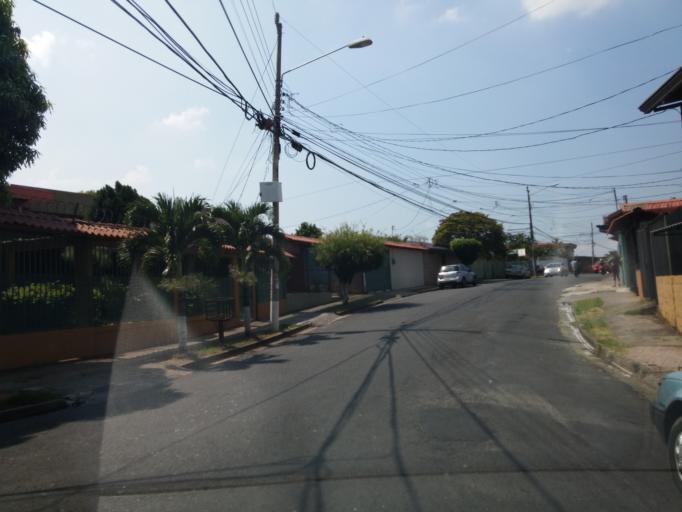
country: CR
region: Alajuela
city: Alajuela
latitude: 10.0152
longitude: -84.2040
